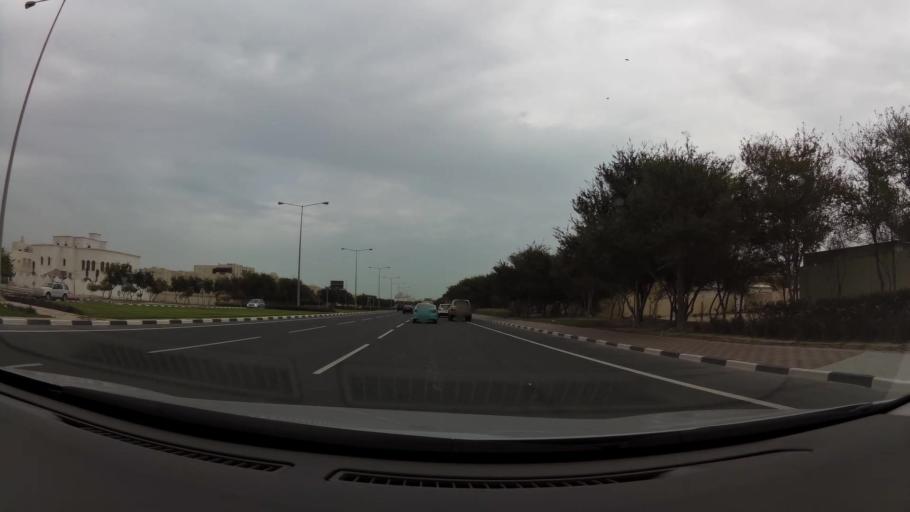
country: QA
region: Baladiyat ad Dawhah
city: Doha
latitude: 25.3483
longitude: 51.4916
